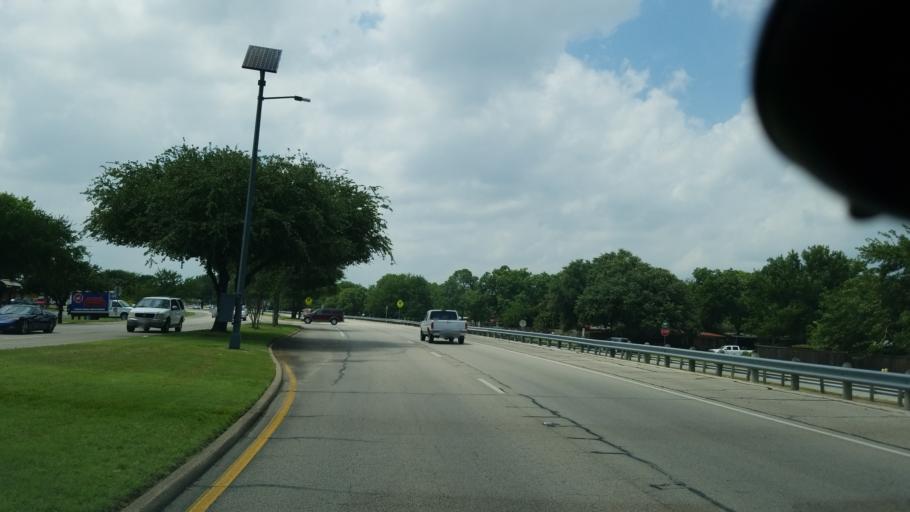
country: US
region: Texas
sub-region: Dallas County
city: Irving
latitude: 32.8238
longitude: -96.9671
